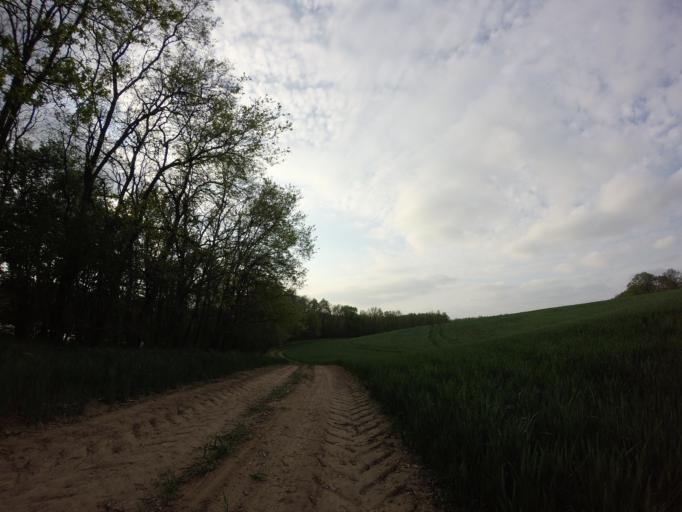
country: PL
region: West Pomeranian Voivodeship
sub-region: Powiat choszczenski
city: Choszczno
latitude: 53.1573
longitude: 15.3444
